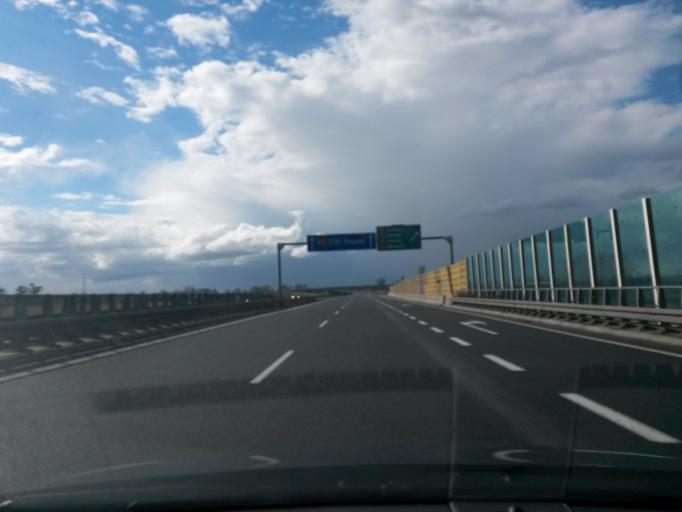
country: PL
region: Greater Poland Voivodeship
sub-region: Powiat wrzesinski
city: Wrzesnia
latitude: 52.3141
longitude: 17.5405
